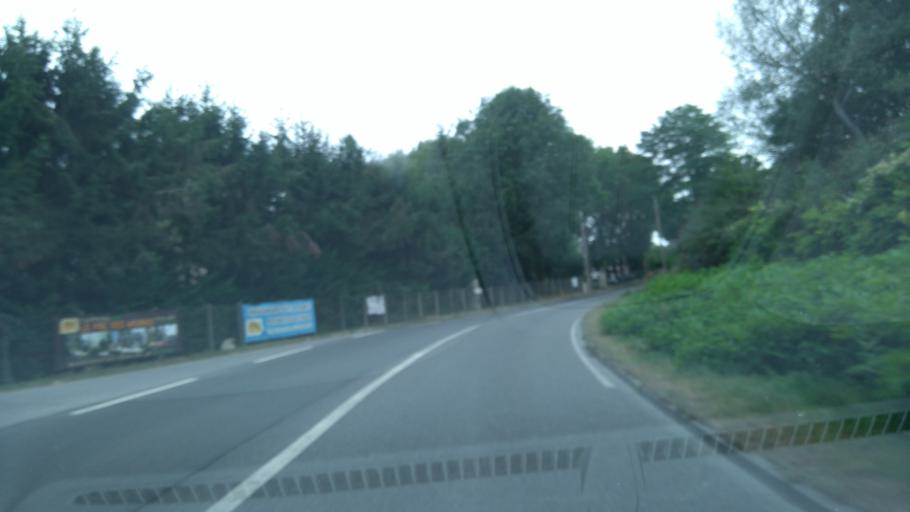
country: FR
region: Picardie
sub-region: Departement de l'Oise
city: Saint-Maximin
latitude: 49.2115
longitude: 2.4285
